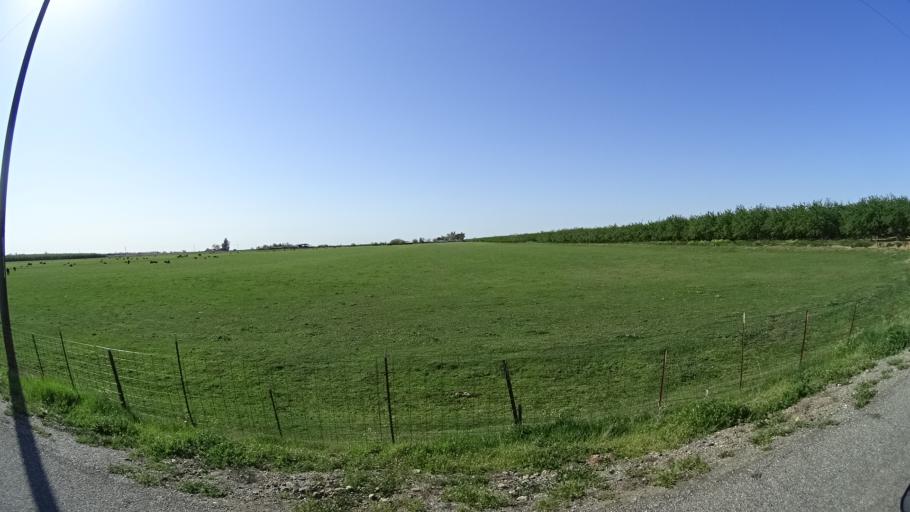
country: US
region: California
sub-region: Glenn County
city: Hamilton City
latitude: 39.7757
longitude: -122.0707
